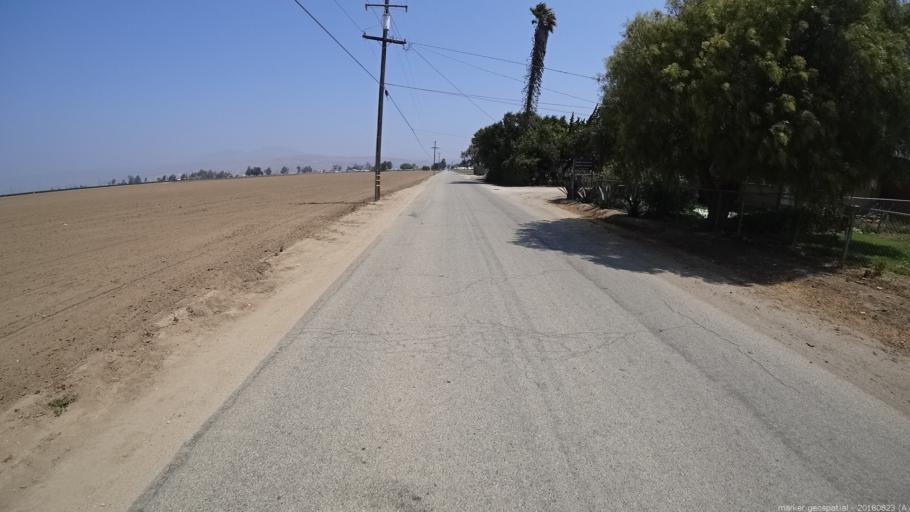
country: US
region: California
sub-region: Monterey County
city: Greenfield
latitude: 36.3293
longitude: -121.2598
